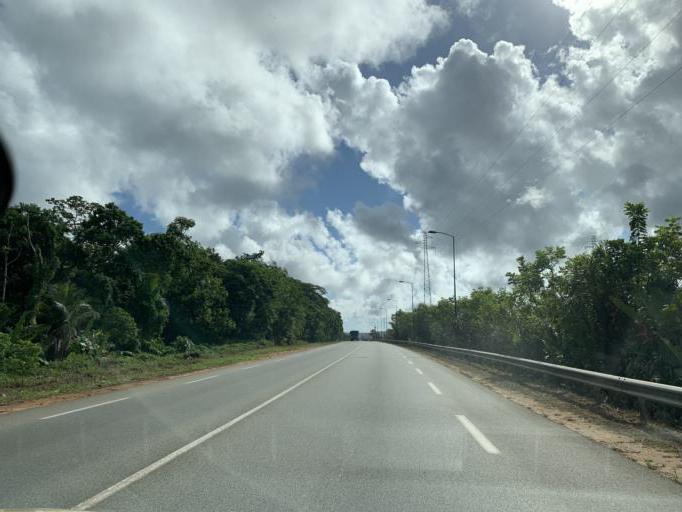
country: GF
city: Macouria
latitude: 4.8918
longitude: -52.3455
